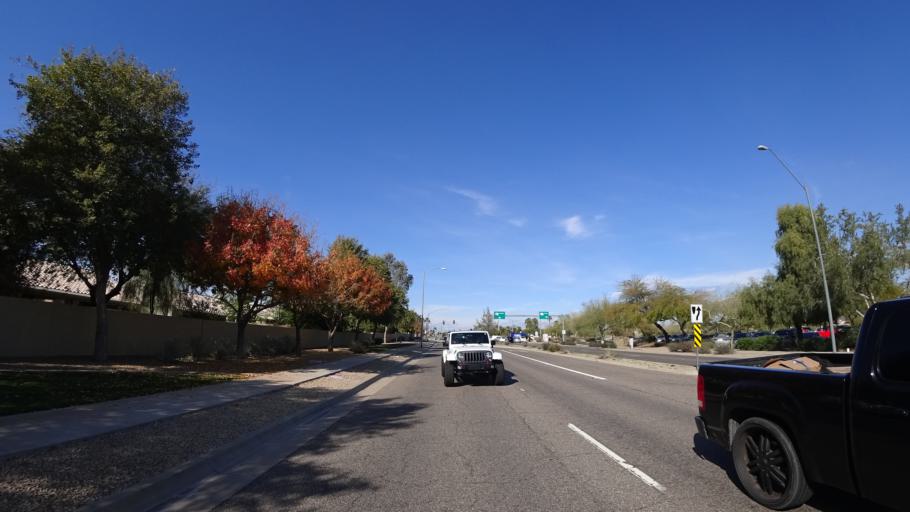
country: US
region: Arizona
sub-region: Maricopa County
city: Sun City
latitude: 33.6660
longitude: -112.2205
